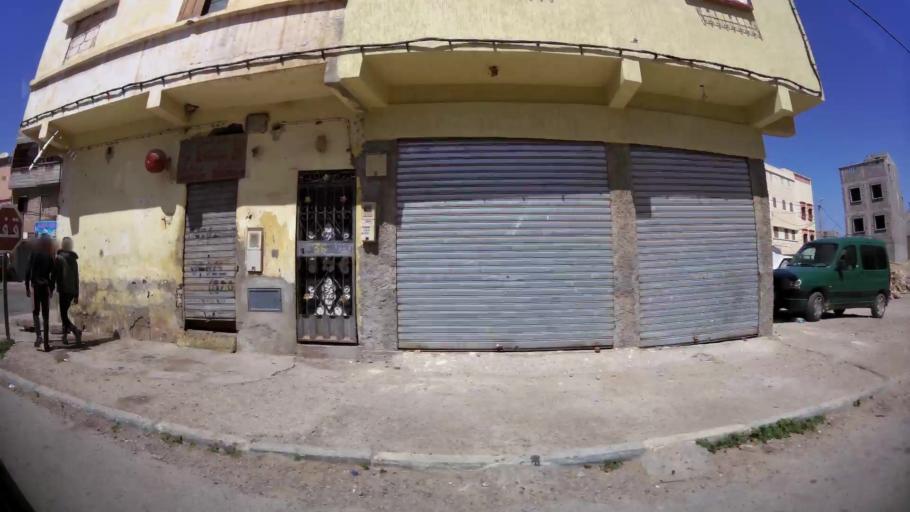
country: MA
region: Souss-Massa-Draa
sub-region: Inezgane-Ait Mellou
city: Inezgane
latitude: 30.3479
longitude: -9.5381
